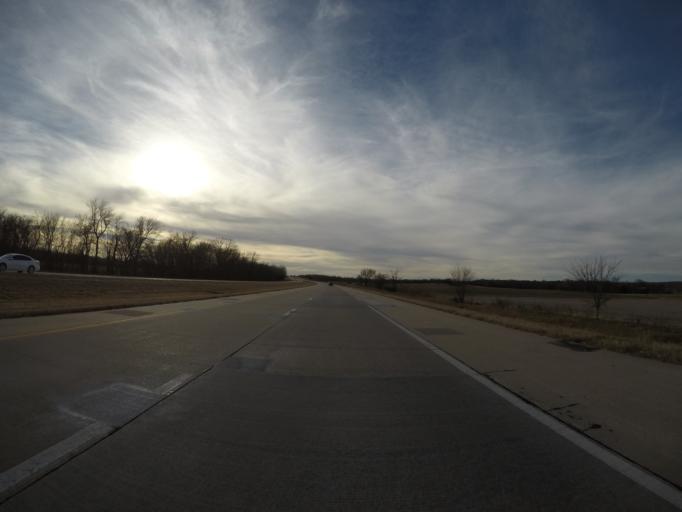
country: US
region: Kansas
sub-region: Franklin County
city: Ottawa
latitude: 38.5563
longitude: -95.3414
